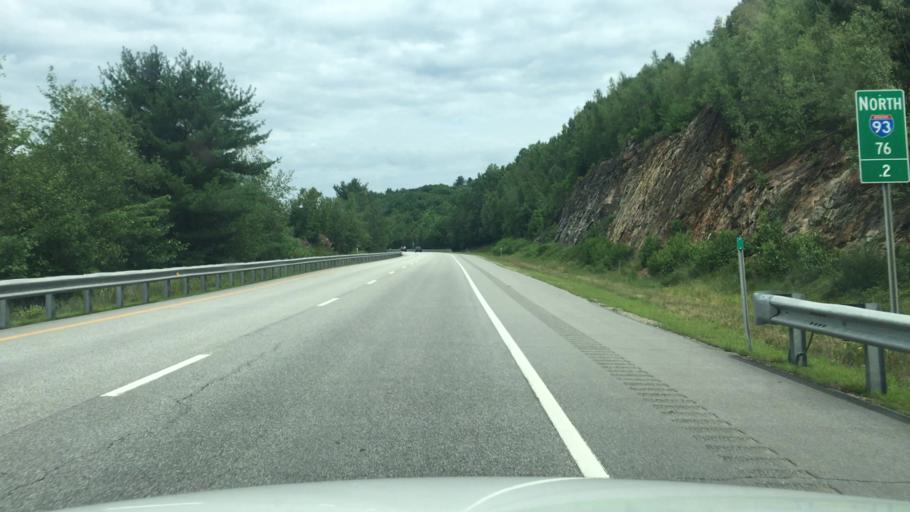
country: US
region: New Hampshire
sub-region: Grafton County
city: Ashland
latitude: 43.7103
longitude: -71.6503
